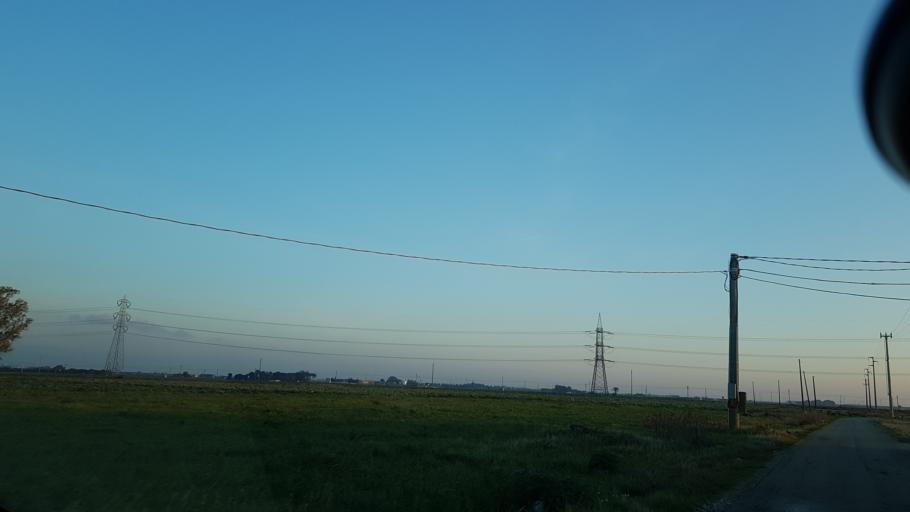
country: IT
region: Apulia
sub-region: Provincia di Brindisi
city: La Rosa
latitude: 40.5963
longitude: 17.9513
